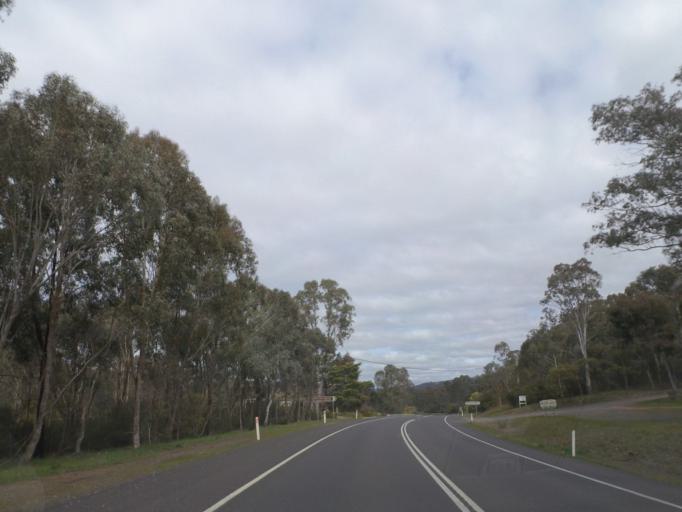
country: AU
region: Victoria
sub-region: Murrindindi
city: Kinglake West
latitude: -37.1433
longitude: 145.2681
